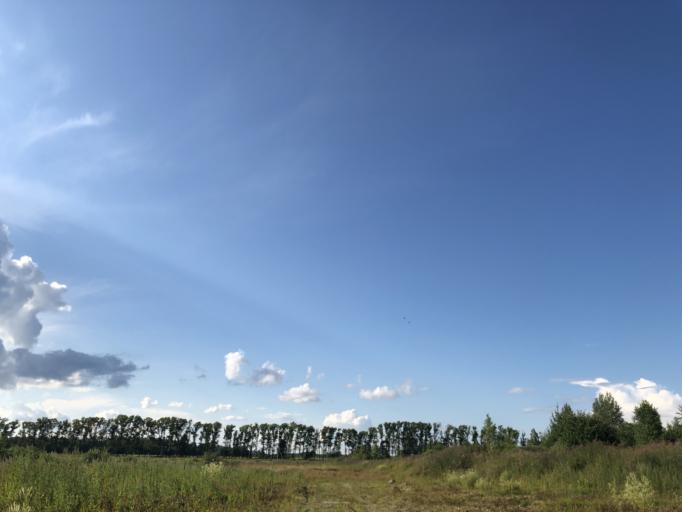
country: RU
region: Tverskaya
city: Rzhev
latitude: 56.2677
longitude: 34.2423
